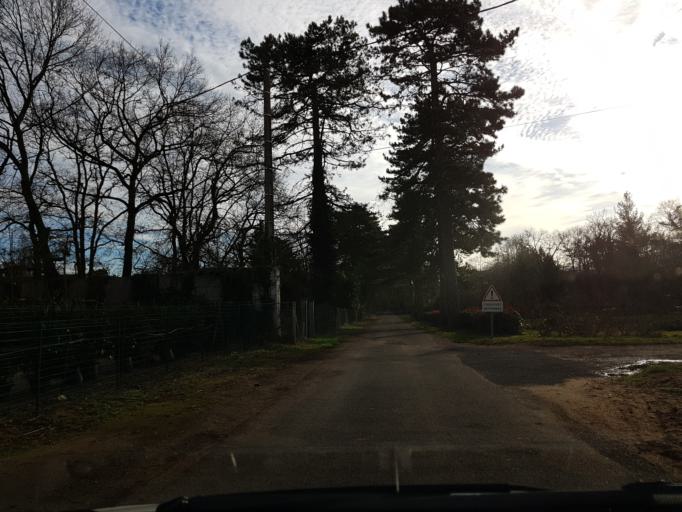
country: FR
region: Centre
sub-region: Departement du Loiret
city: Checy
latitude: 47.8830
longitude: 1.9950
